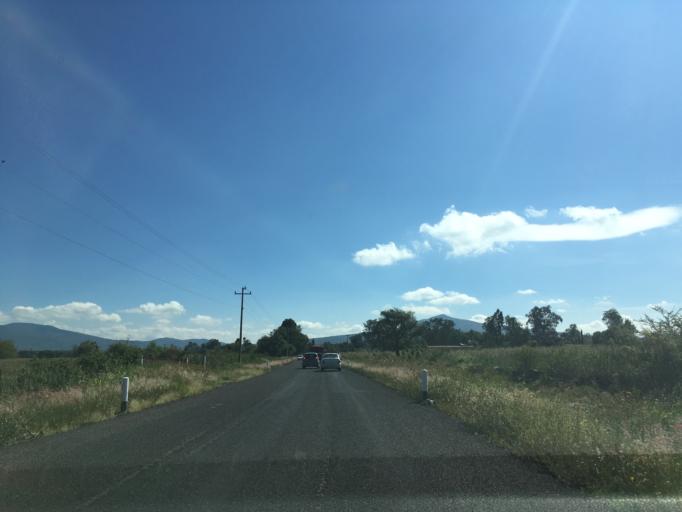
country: MX
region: Mexico
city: Tlazazalca
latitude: 19.9720
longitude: -102.0961
